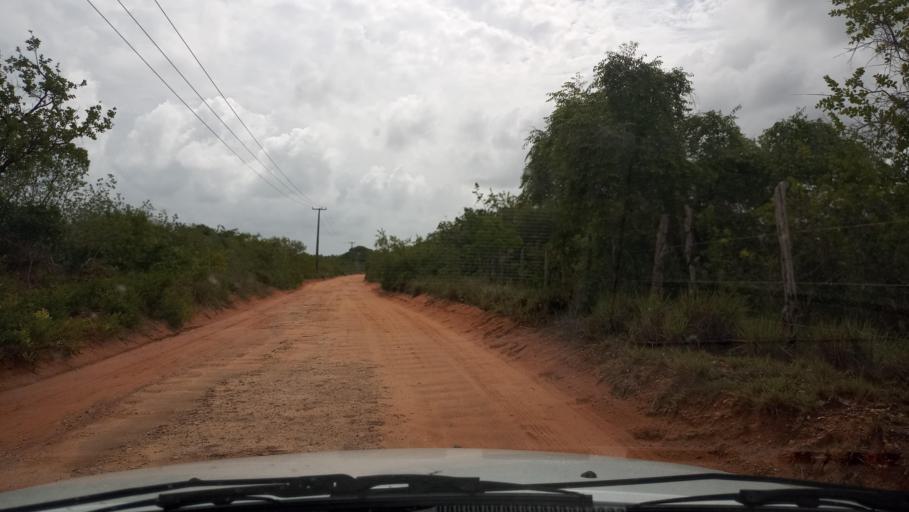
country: BR
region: Rio Grande do Norte
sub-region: Maxaranguape
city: Sao Miguel
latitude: -5.4832
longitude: -35.3214
